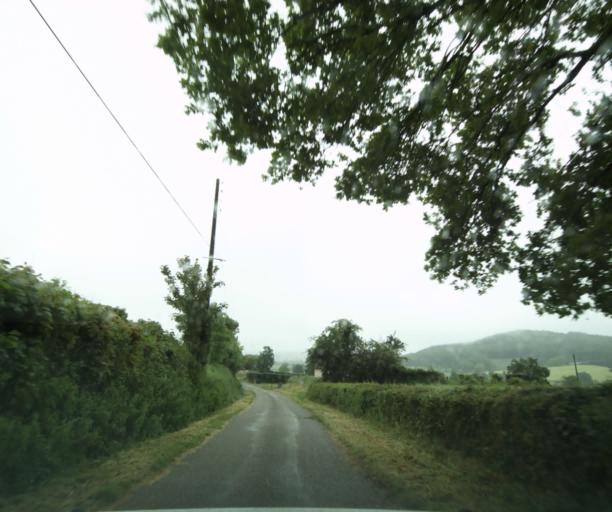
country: FR
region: Bourgogne
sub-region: Departement de Saone-et-Loire
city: Charolles
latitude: 46.4016
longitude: 4.3765
